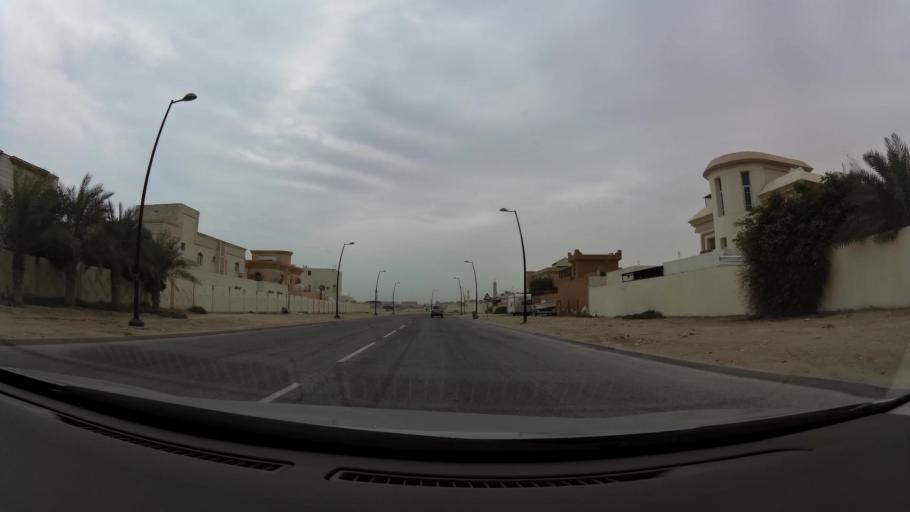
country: QA
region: Baladiyat ad Dawhah
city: Doha
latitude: 25.3478
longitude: 51.4999
